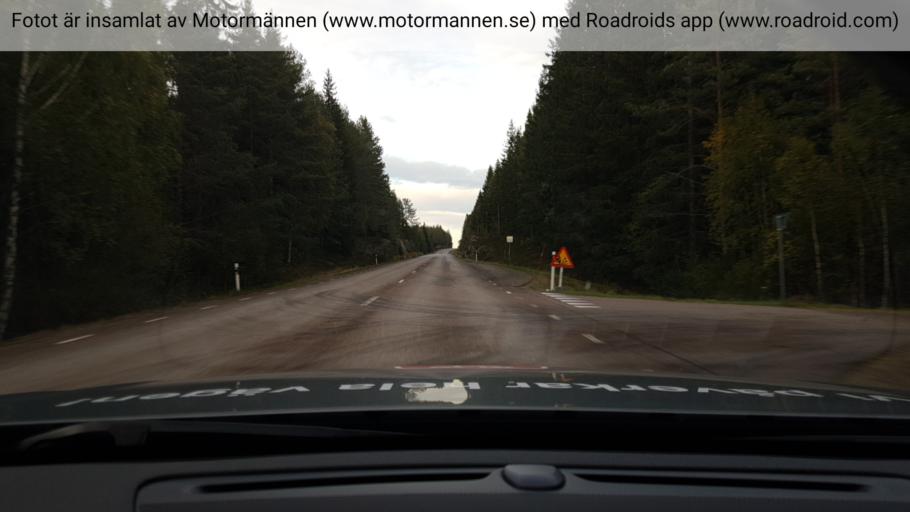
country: SE
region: Vaestra Goetaland
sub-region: Amals Kommun
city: Amal
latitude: 59.0652
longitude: 12.5488
